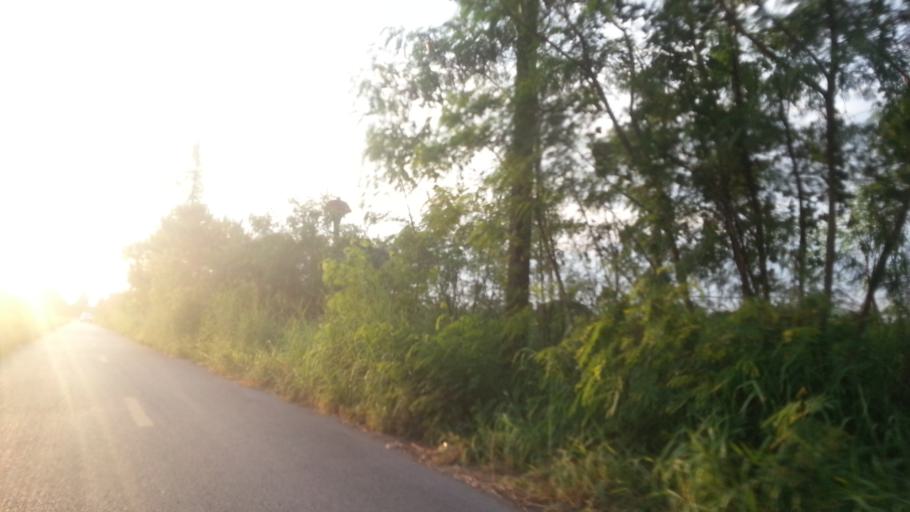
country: TH
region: Pathum Thani
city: Ban Rangsit
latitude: 14.0410
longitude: 100.8503
